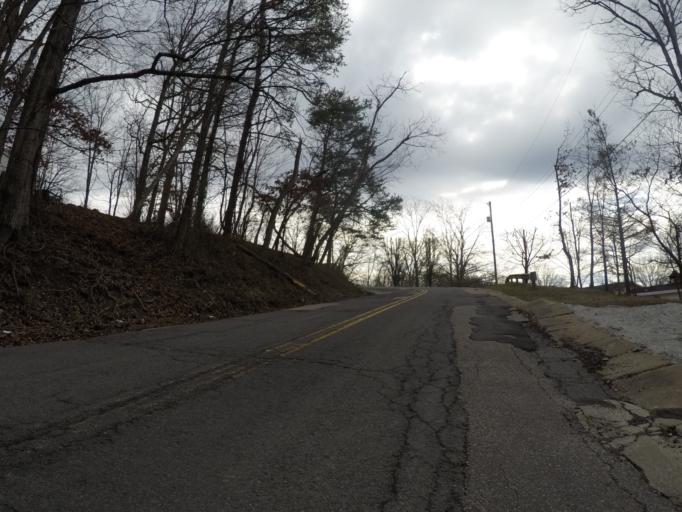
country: US
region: West Virginia
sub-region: Cabell County
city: Pea Ridge
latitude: 38.3940
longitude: -82.3810
